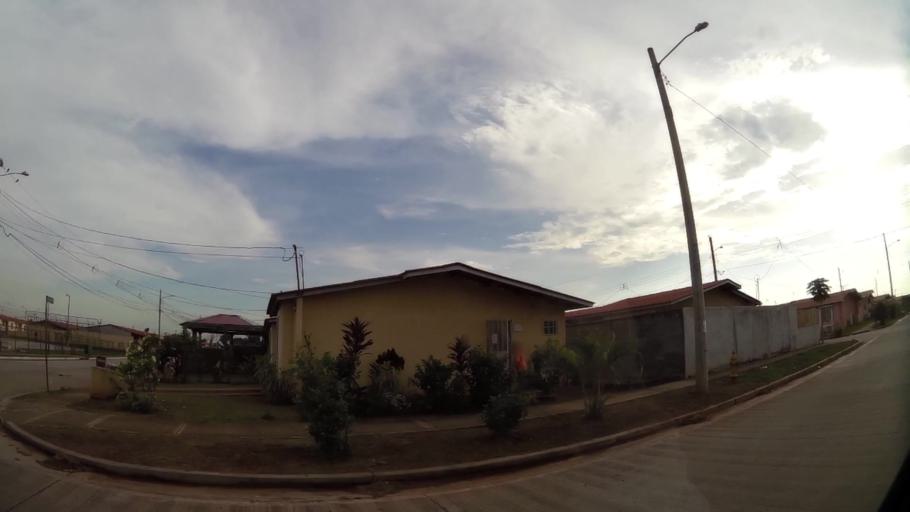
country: PA
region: Panama
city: Tocumen
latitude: 9.0755
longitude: -79.3579
